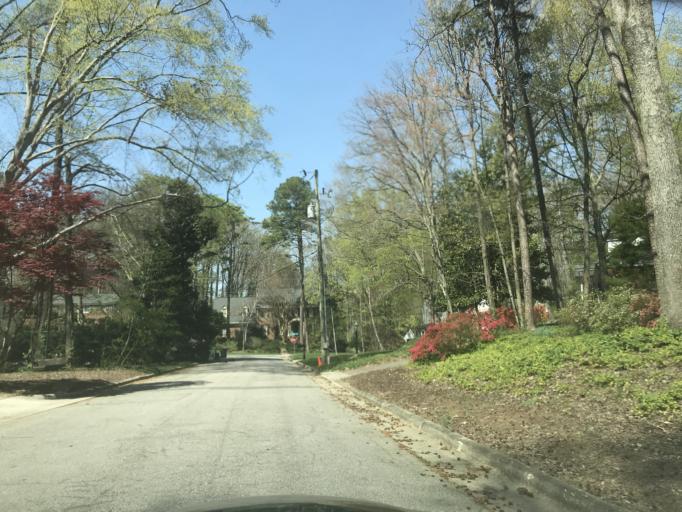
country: US
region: North Carolina
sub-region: Wake County
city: West Raleigh
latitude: 35.8309
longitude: -78.6445
